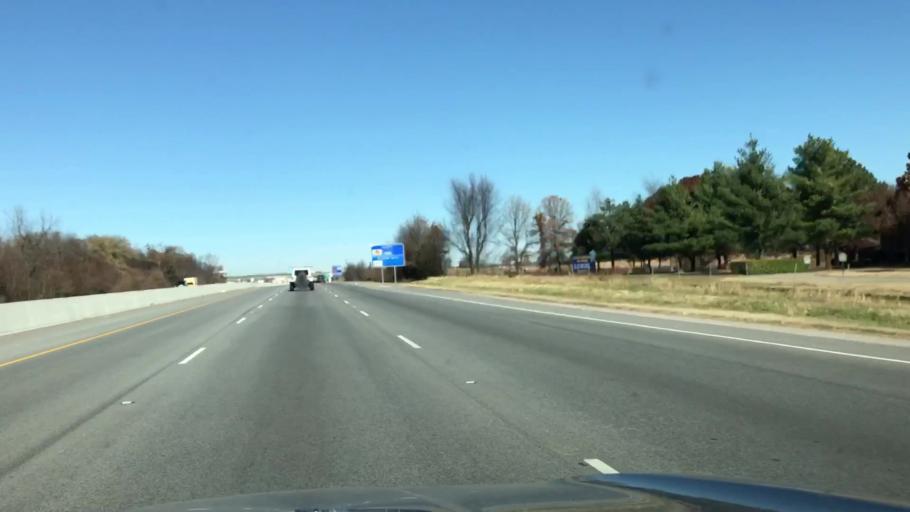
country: US
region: Arkansas
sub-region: Benton County
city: Lowell
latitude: 36.2607
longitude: -94.1502
